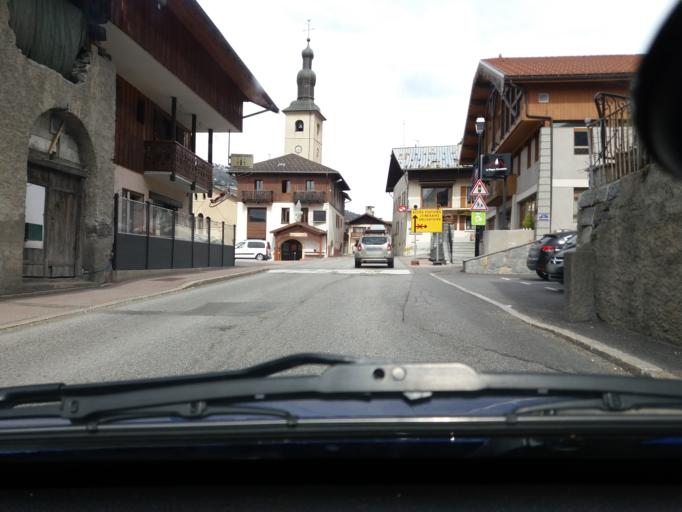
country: FR
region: Rhone-Alpes
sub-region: Departement de la Savoie
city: Macot-la-Plagne
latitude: 45.5531
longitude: 6.6715
